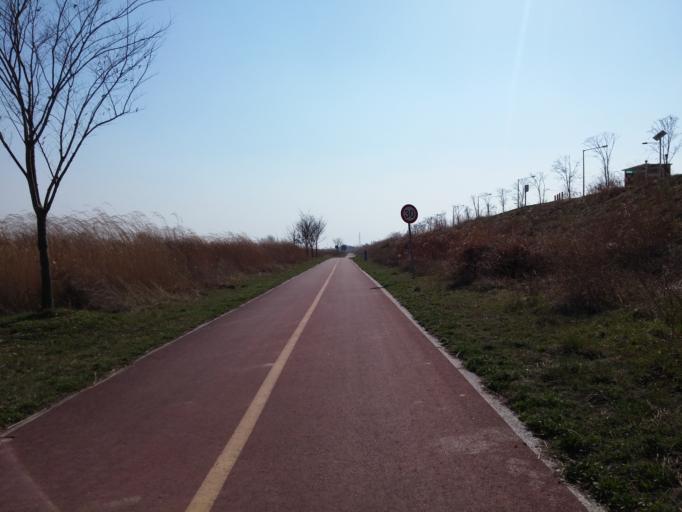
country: KR
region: Chungcheongbuk-do
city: Cheongju-si
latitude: 36.6477
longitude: 127.3681
